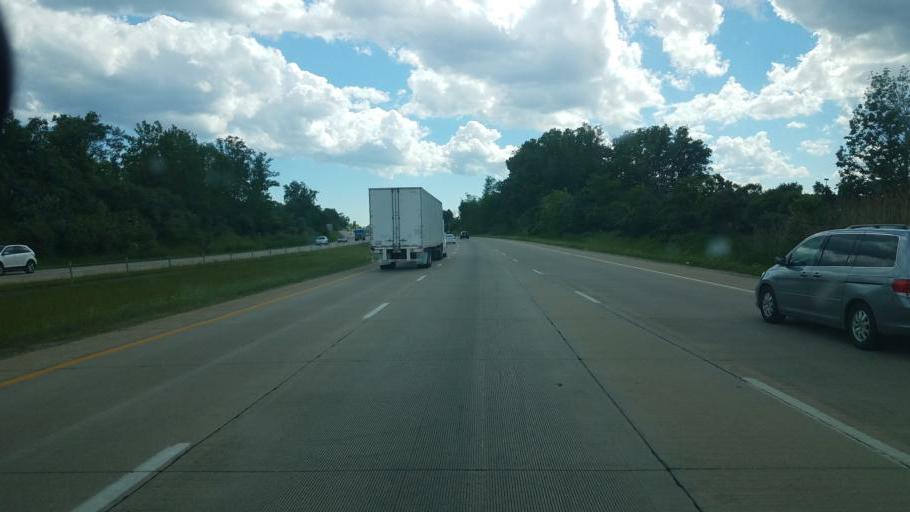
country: US
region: Ohio
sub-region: Portage County
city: Brimfield
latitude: 41.0973
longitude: -81.3804
